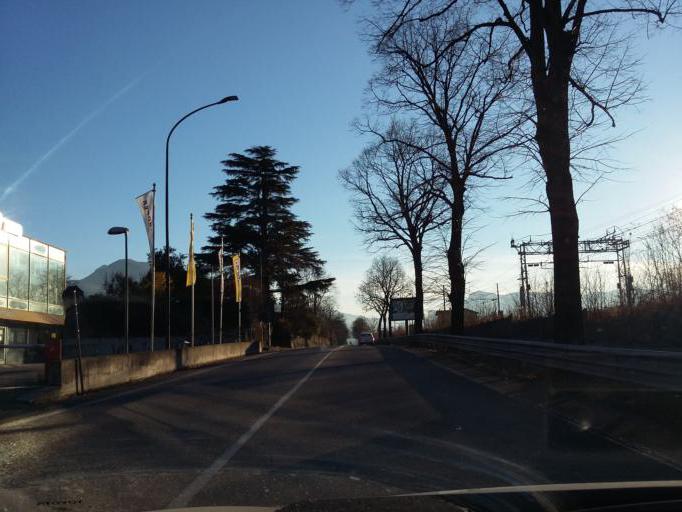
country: IT
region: Trentino-Alto Adige
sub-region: Provincia di Trento
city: Nogaredo
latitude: 45.8997
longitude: 11.0355
